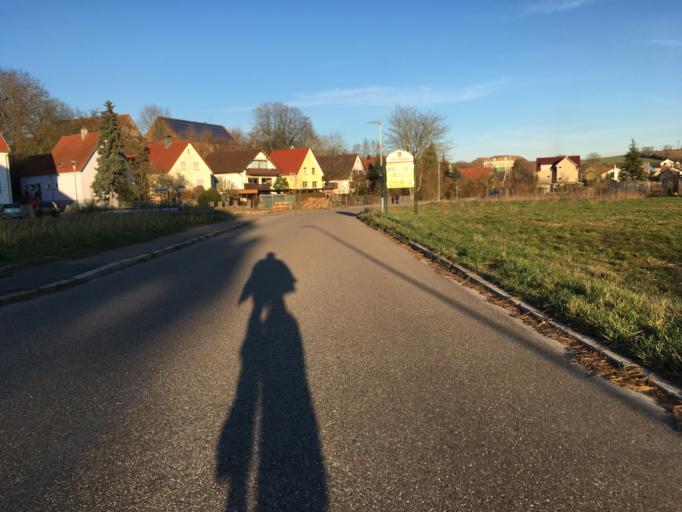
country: DE
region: Baden-Wuerttemberg
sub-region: Regierungsbezirk Stuttgart
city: Ittlingen
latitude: 49.1885
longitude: 8.9288
